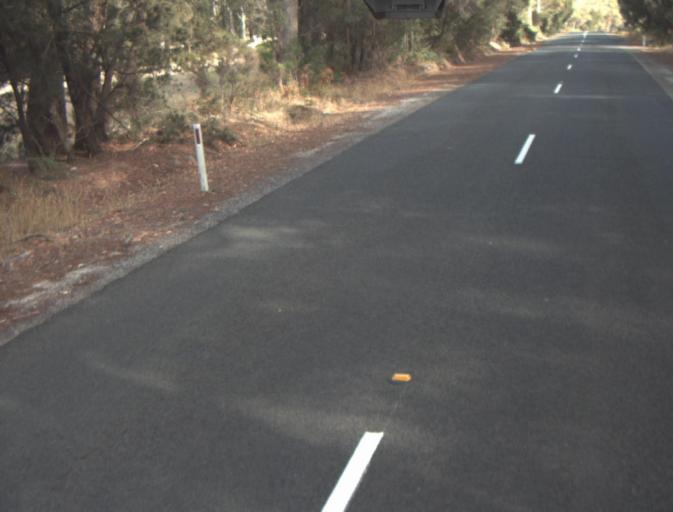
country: AU
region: Tasmania
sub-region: Dorset
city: Bridport
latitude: -41.1212
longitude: 147.2054
